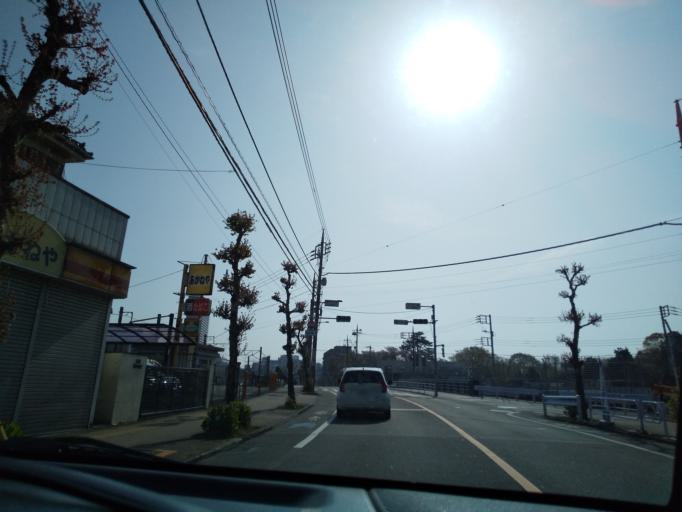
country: JP
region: Tokyo
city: Hino
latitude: 35.6972
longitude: 139.4045
